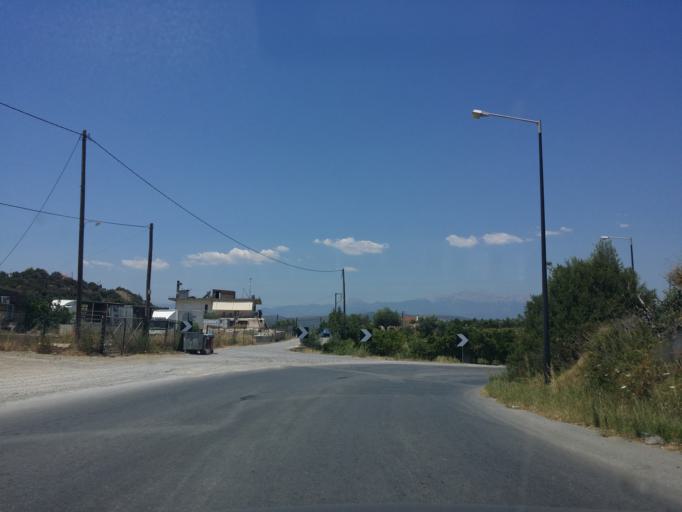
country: GR
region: Peloponnese
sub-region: Nomos Lakonias
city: Vlakhiotis
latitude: 36.8611
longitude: 22.7186
